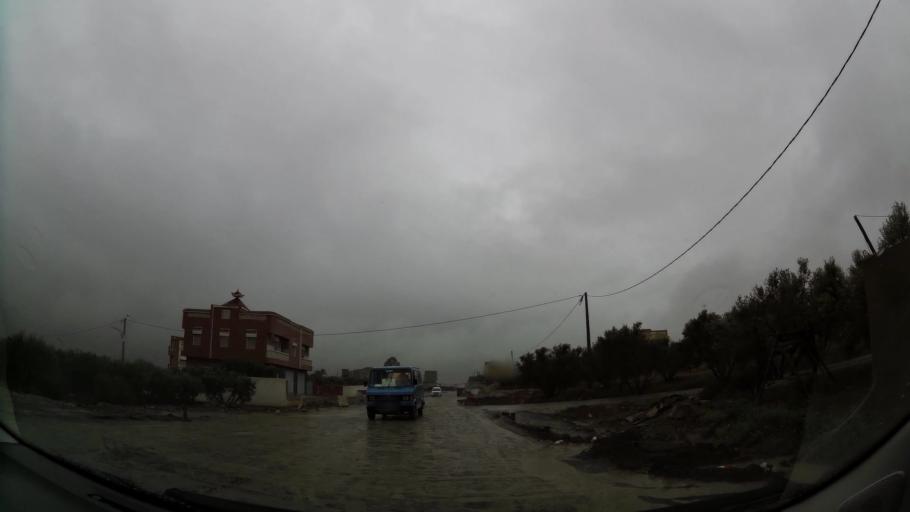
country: MA
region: Oriental
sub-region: Nador
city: Midar
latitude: 34.8734
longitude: -3.7259
